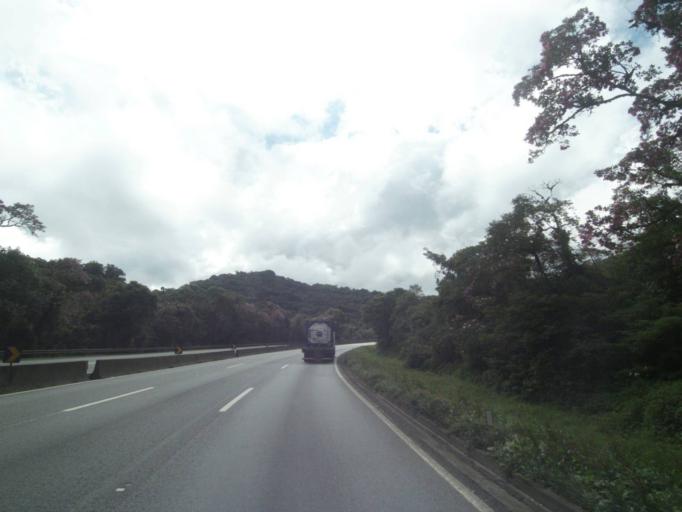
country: BR
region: Parana
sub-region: Piraquara
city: Piraquara
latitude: -25.5969
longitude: -48.9041
